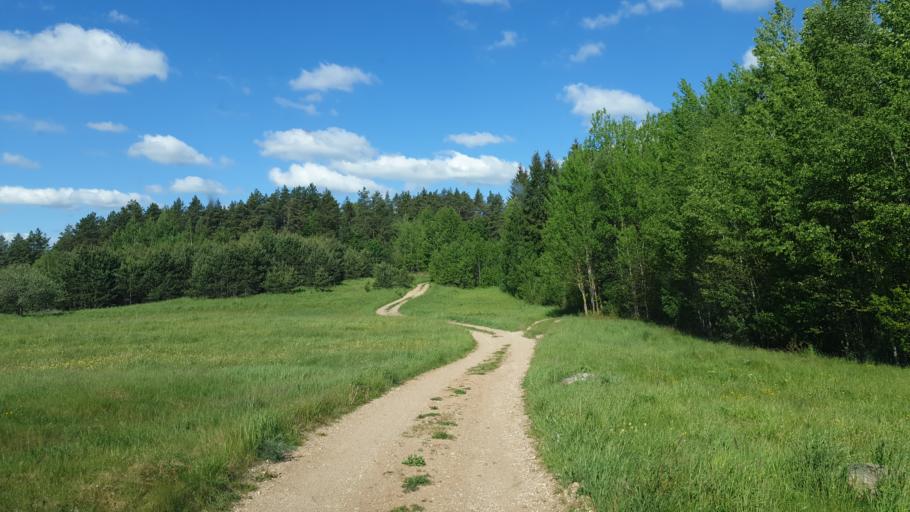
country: LT
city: Aukstadvaris
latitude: 54.5821
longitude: 24.4515
